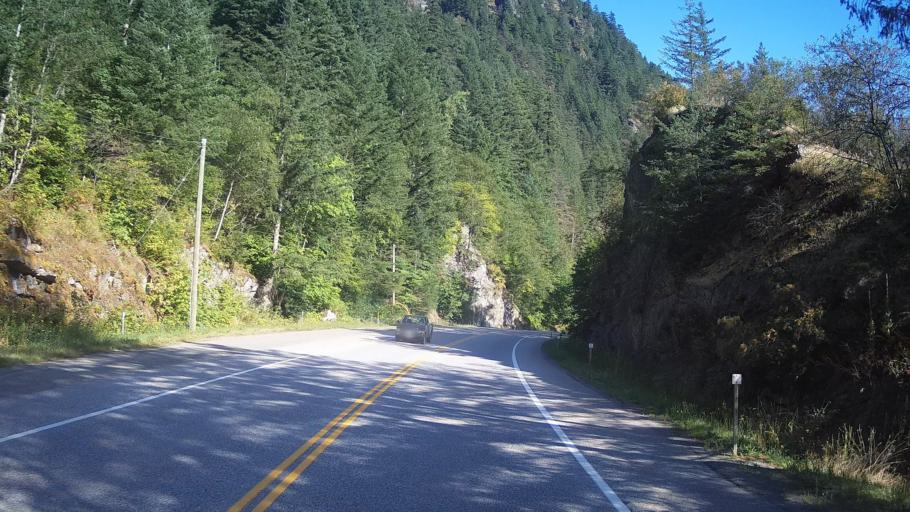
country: CA
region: British Columbia
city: Hope
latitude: 49.5687
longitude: -121.4026
